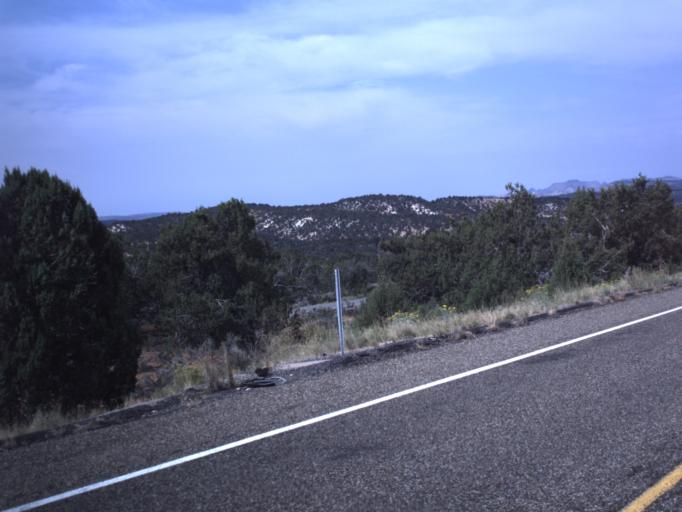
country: US
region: Utah
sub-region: Kane County
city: Kanab
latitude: 37.1871
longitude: -112.6535
